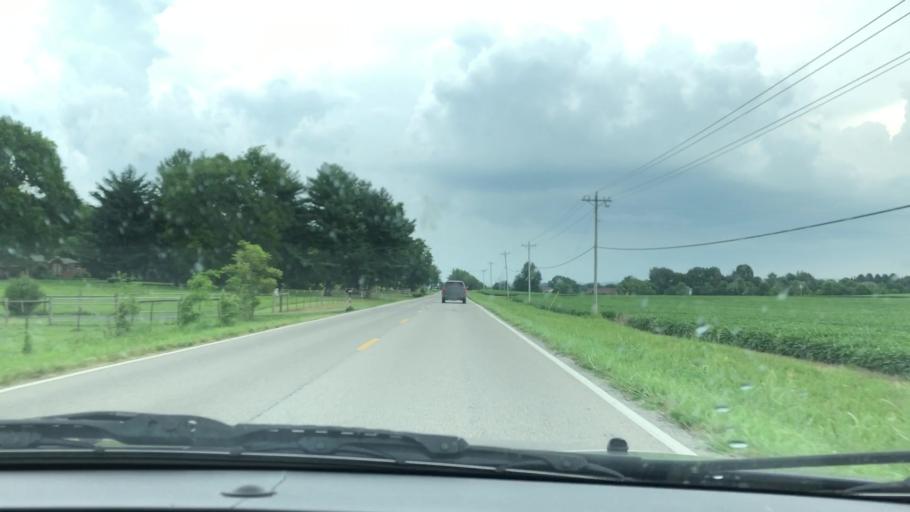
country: US
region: Tennessee
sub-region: Maury County
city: Spring Hill
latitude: 35.7130
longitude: -87.0147
